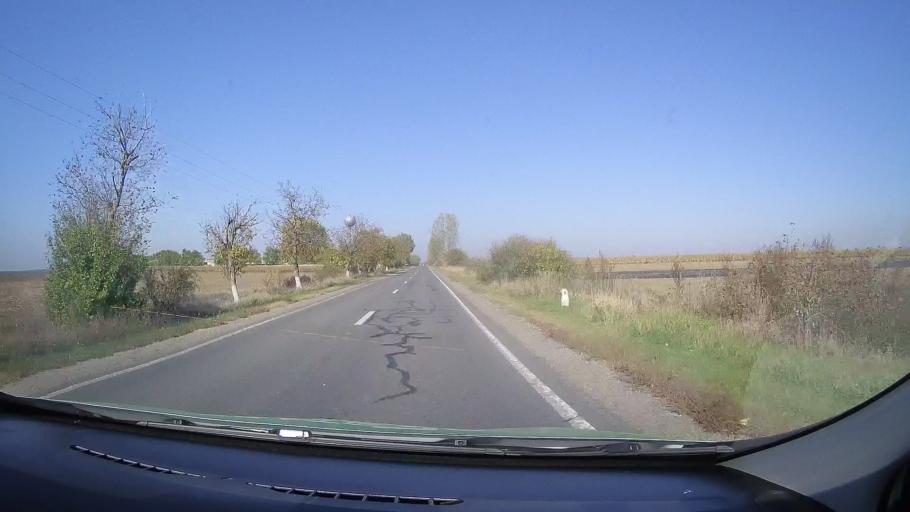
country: RO
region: Satu Mare
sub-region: Comuna Urziceni
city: Urziceni
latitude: 47.7201
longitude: 22.4169
